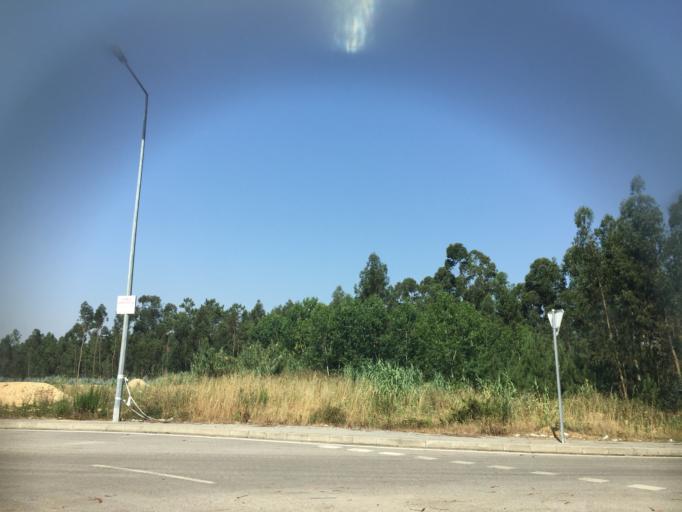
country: PT
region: Coimbra
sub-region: Cantanhede
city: Cantanhede
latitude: 40.4273
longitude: -8.5454
